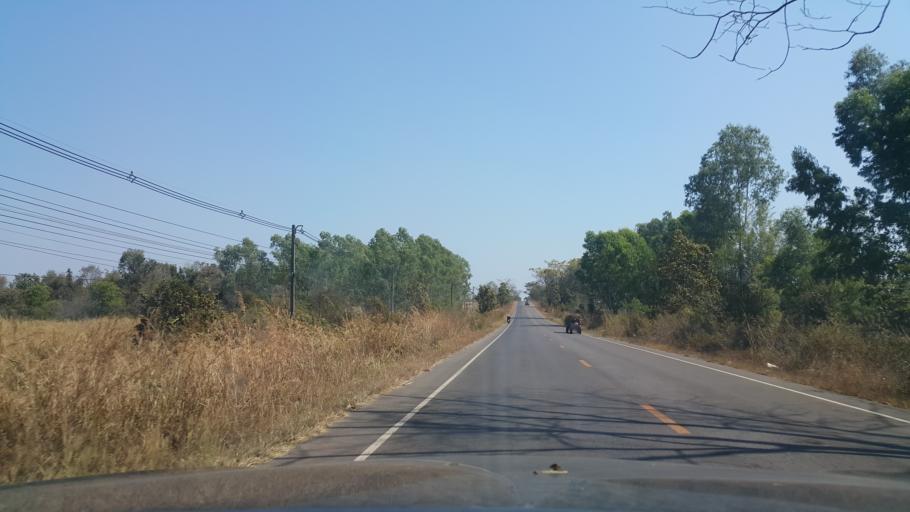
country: TH
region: Changwat Udon Thani
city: Ban Dung
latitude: 17.6086
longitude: 103.2672
